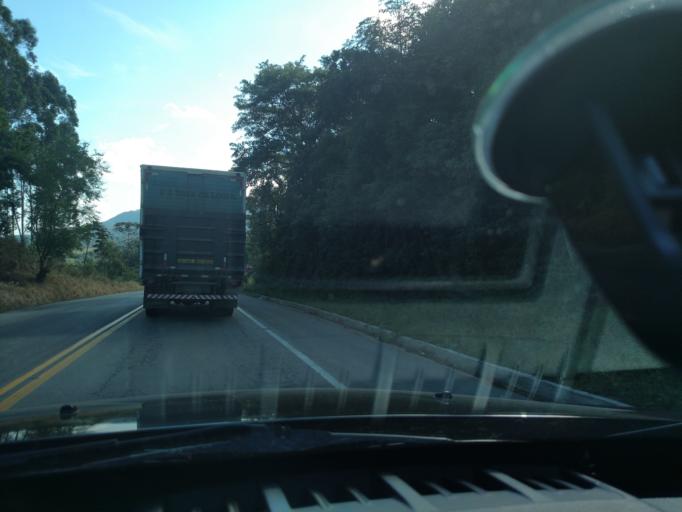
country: BR
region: Santa Catarina
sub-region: Ibirama
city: Ibirama
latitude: -27.1135
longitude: -49.5296
